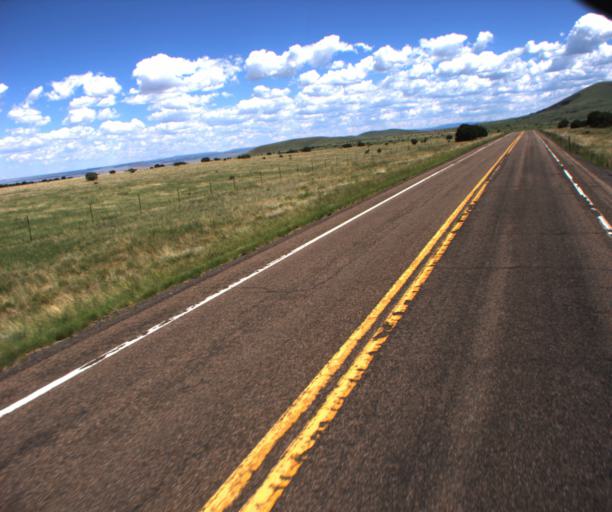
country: US
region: Arizona
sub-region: Apache County
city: Springerville
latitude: 34.2527
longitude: -109.5414
